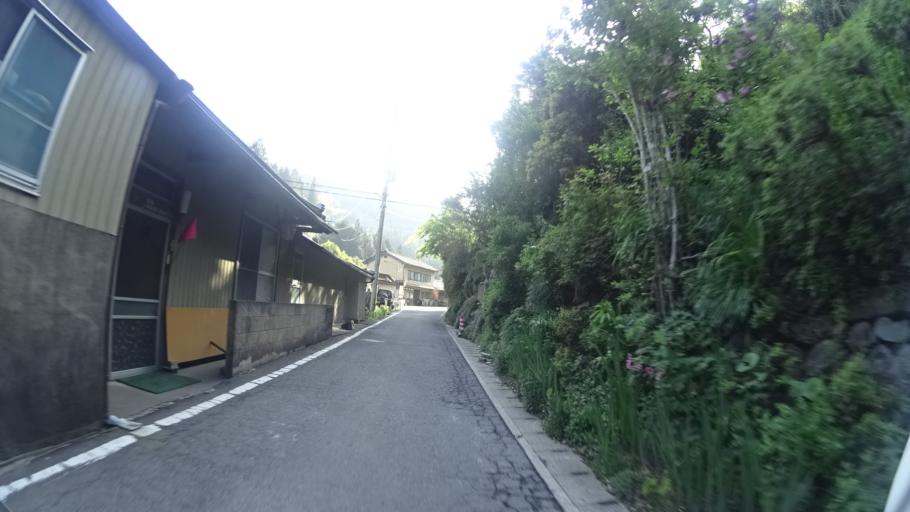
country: JP
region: Tokushima
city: Ikedacho
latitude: 33.8804
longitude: 133.9370
